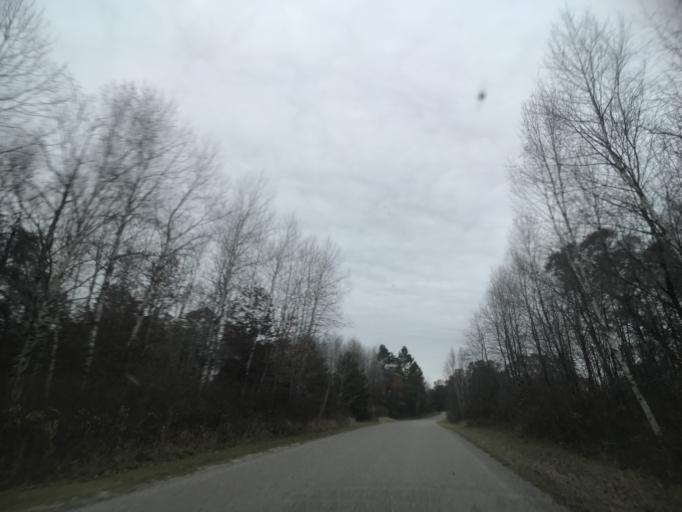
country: US
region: Wisconsin
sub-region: Oconto County
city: Gillett
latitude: 45.3496
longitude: -88.2859
